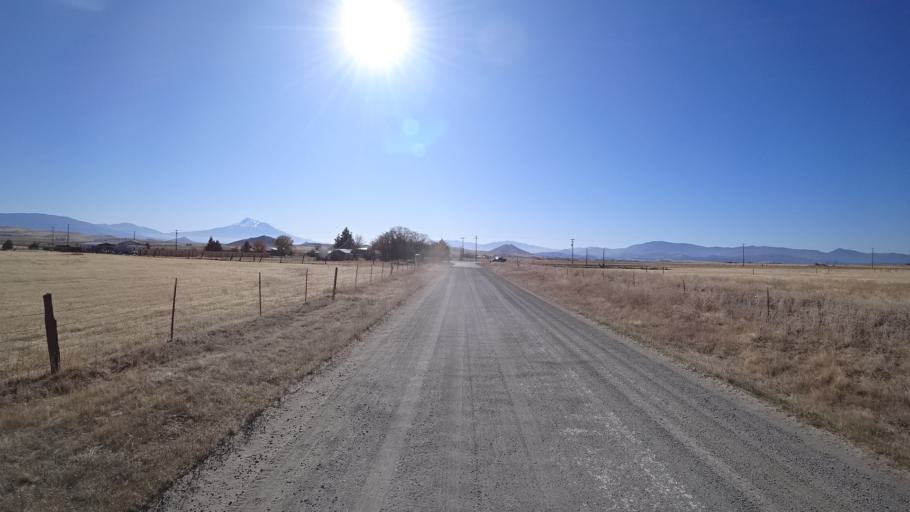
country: US
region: California
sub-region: Siskiyou County
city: Montague
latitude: 41.7720
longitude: -122.5052
